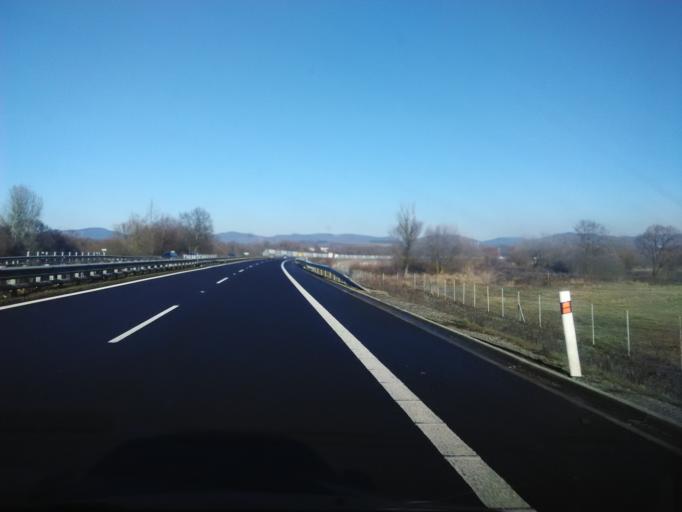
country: SK
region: Banskobystricky
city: Ziar nad Hronom
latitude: 48.5610
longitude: 18.8202
